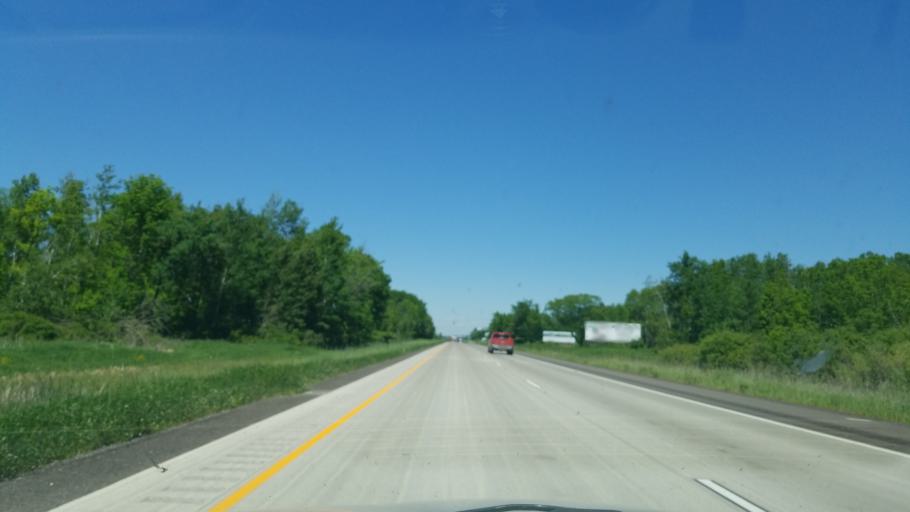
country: US
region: Minnesota
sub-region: Pine County
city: Pine City
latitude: 45.8795
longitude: -92.9686
